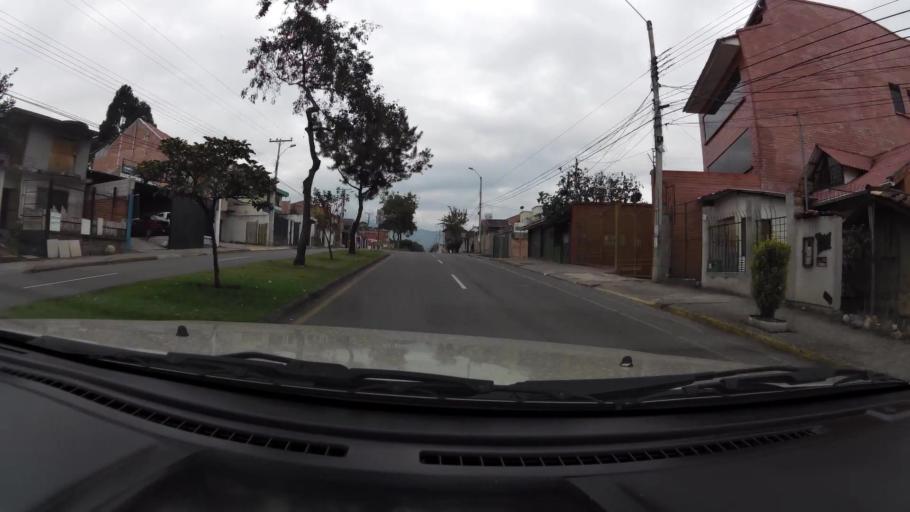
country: EC
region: Azuay
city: Cuenca
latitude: -2.9082
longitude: -79.0177
